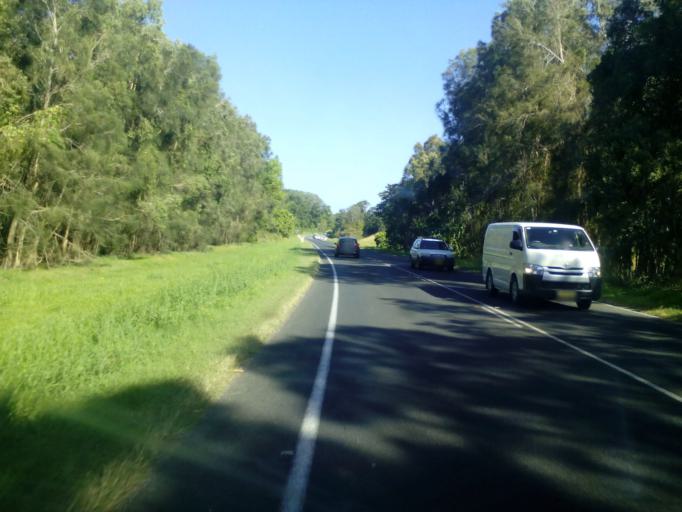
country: AU
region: New South Wales
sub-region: Tweed
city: Kingscliff
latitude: -28.2582
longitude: 153.5601
